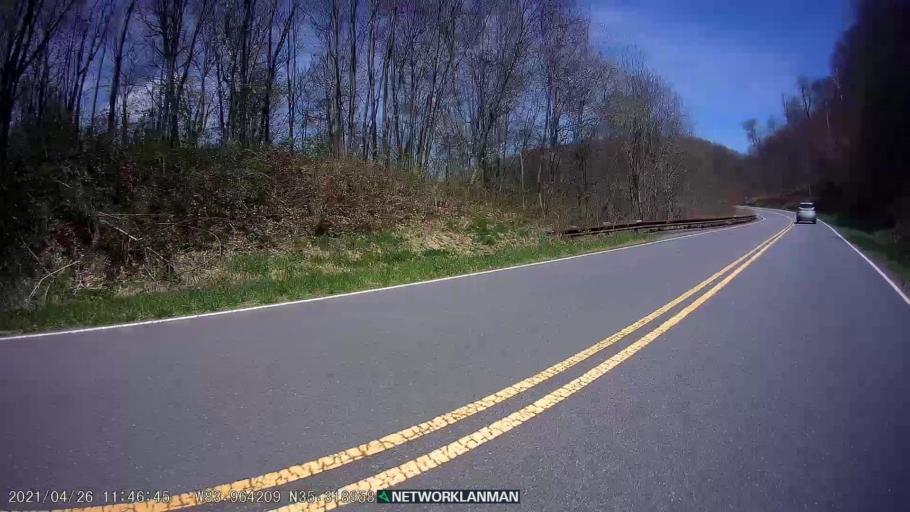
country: US
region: North Carolina
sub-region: Graham County
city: Robbinsville
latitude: 35.3190
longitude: -83.9638
